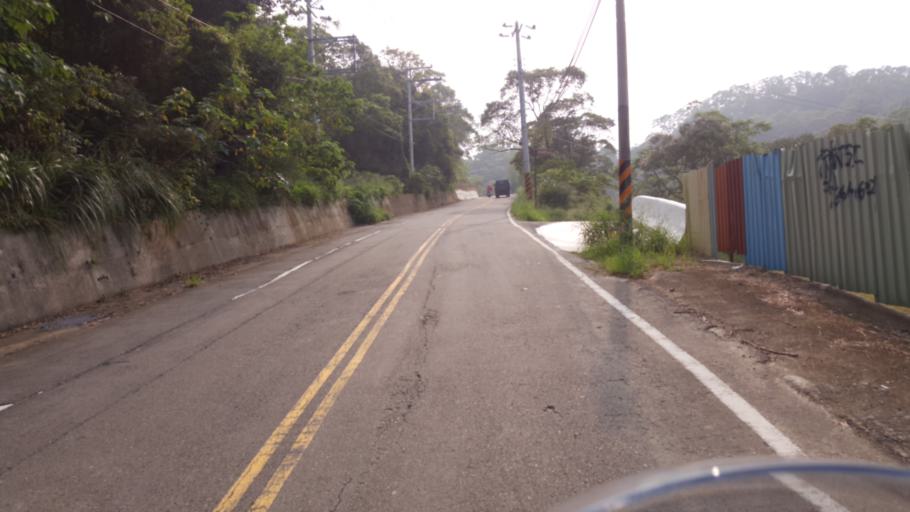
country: TW
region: Taiwan
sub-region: Hsinchu
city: Hsinchu
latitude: 24.7272
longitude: 120.9611
